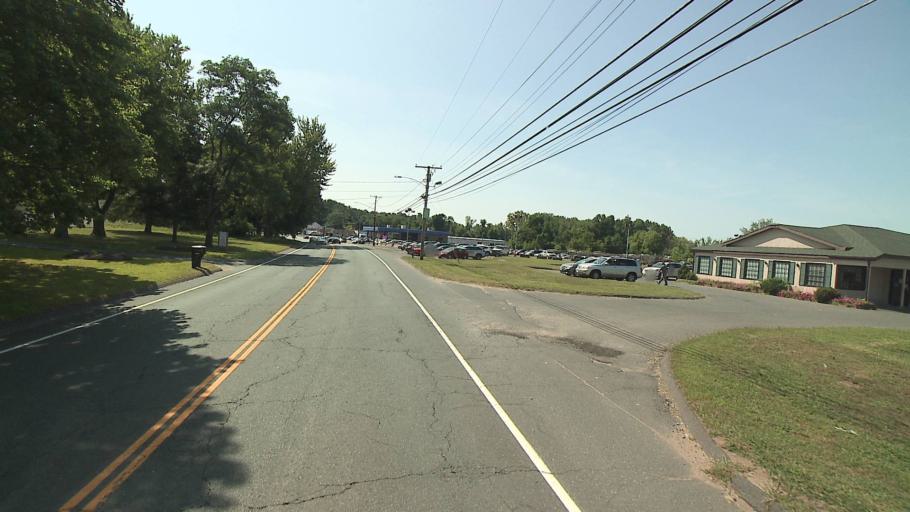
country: US
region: Connecticut
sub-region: Hartford County
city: Windsor
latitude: 41.8773
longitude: -72.6095
